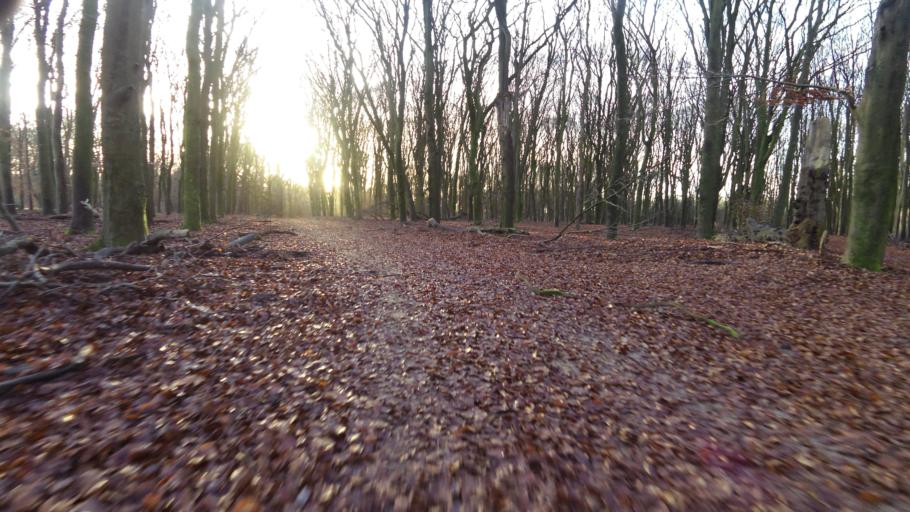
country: NL
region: Gelderland
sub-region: Gemeente Apeldoorn
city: Uddel
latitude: 52.2185
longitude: 5.8643
